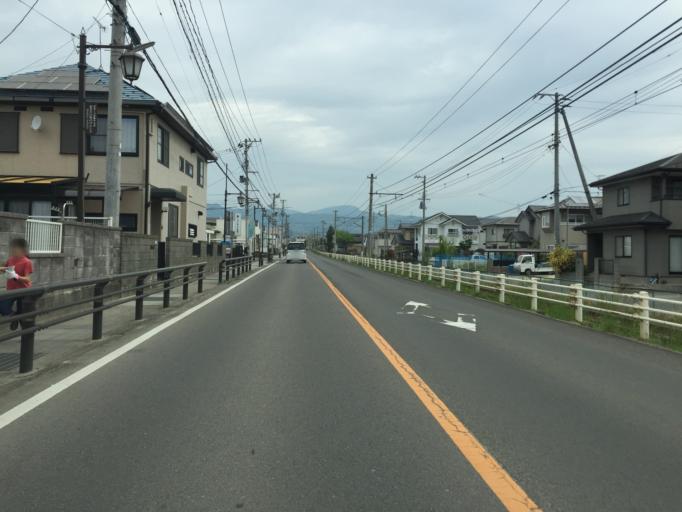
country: JP
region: Fukushima
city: Fukushima-shi
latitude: 37.8073
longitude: 140.4433
